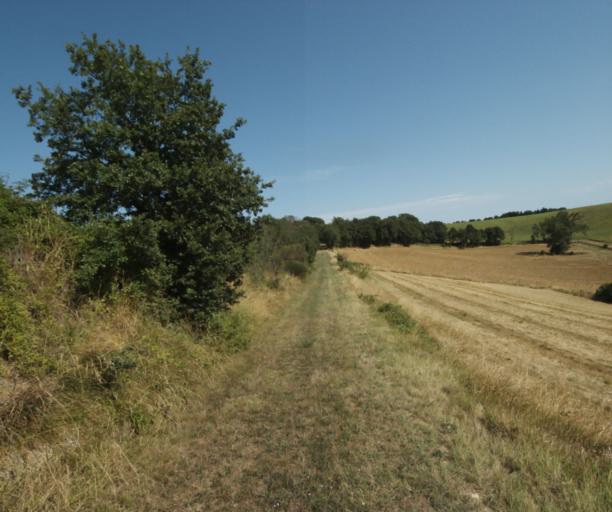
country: FR
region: Midi-Pyrenees
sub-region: Departement de la Haute-Garonne
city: Saint-Felix-Lauragais
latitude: 43.4378
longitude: 1.8556
